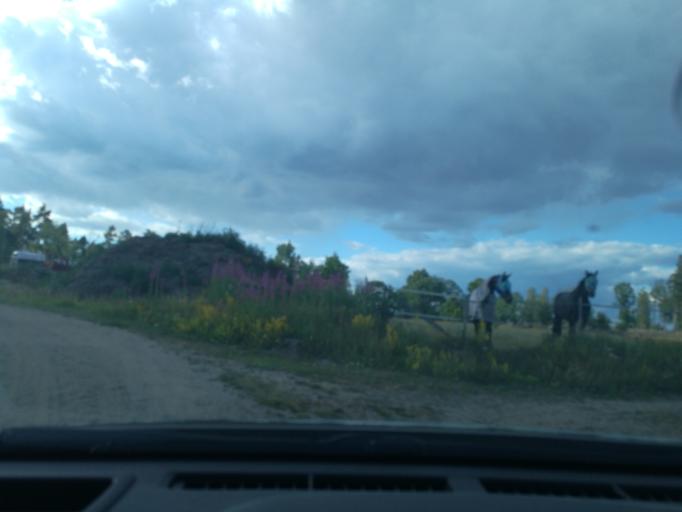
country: SE
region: Soedermanland
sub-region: Eskilstuna Kommun
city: Arla
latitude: 59.3819
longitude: 16.6870
